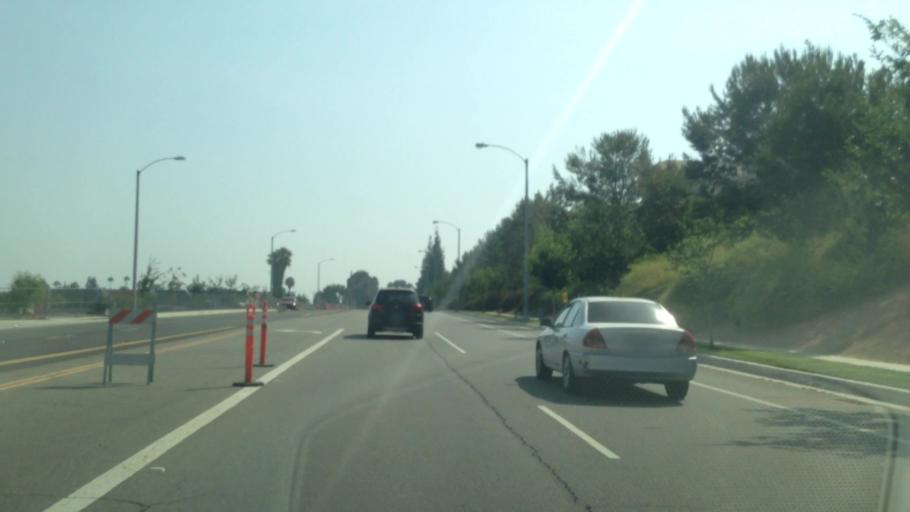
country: US
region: California
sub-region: Riverside County
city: Home Gardens
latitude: 33.8990
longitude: -117.4680
